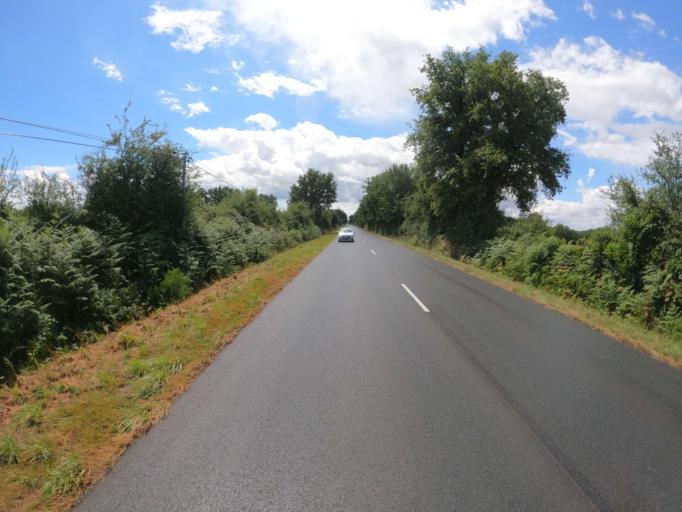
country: FR
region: Pays de la Loire
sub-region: Departement de Maine-et-Loire
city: Feneu
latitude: 47.6049
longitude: -0.5867
